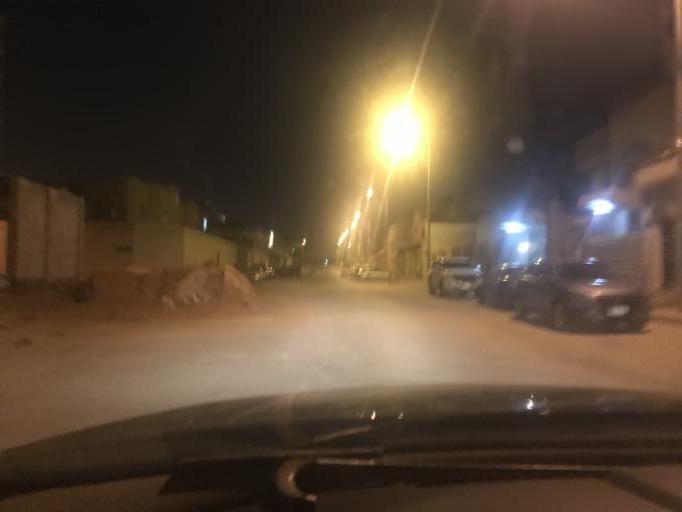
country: SA
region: Ar Riyad
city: Riyadh
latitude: 24.7567
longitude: 46.7629
